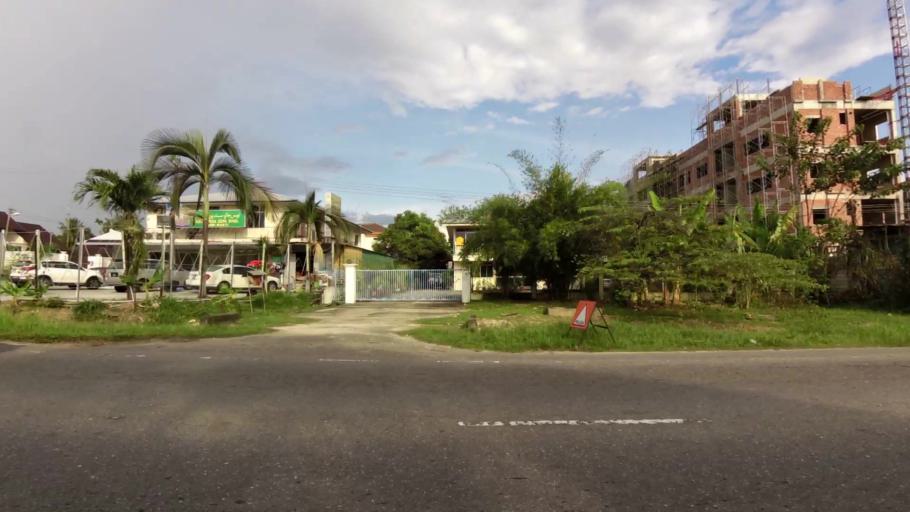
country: BN
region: Brunei and Muara
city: Bandar Seri Begawan
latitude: 4.9688
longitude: 114.9775
